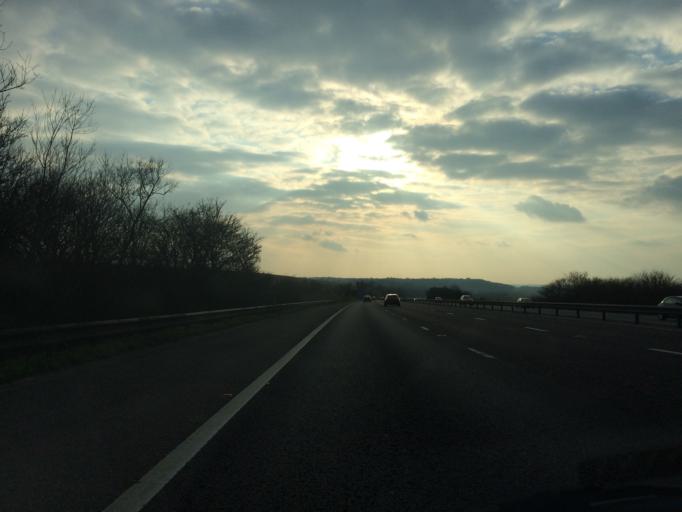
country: GB
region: England
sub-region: Borough of Swindon
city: Wanborough
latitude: 51.5258
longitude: -1.6990
